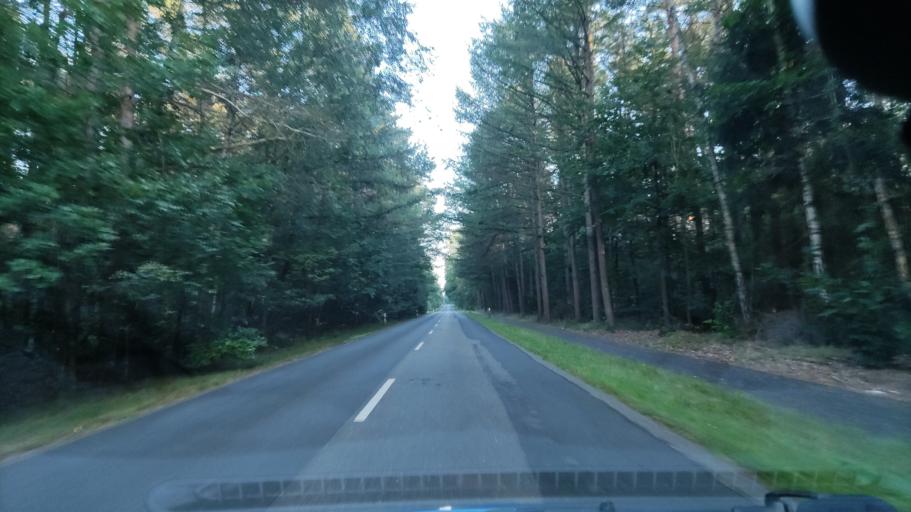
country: DE
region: Lower Saxony
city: Munster
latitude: 52.9715
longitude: 10.1526
